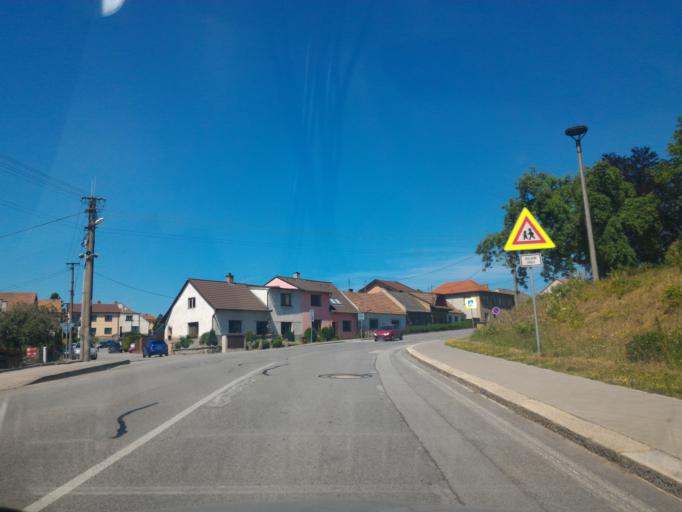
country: CZ
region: Vysocina
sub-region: Okres Jihlava
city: Trest'
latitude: 49.2712
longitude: 15.4748
